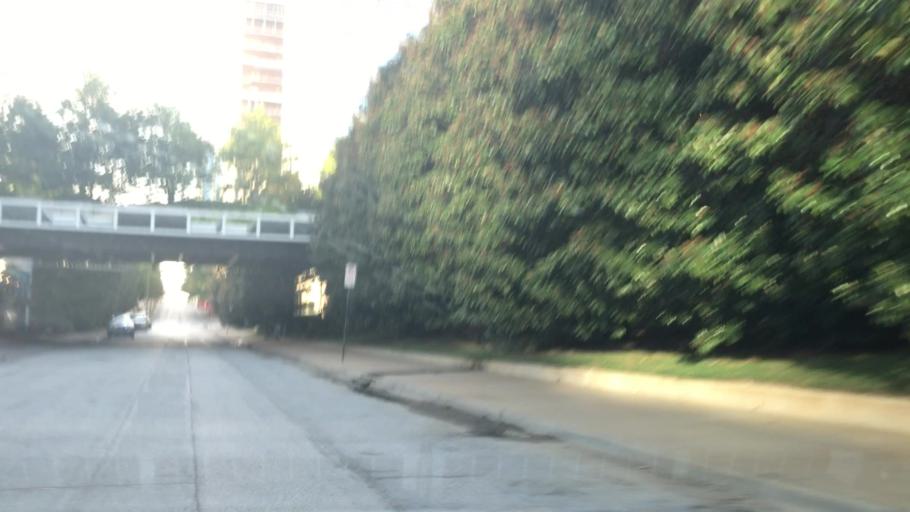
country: US
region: Texas
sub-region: Dallas County
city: Dallas
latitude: 32.7930
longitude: -96.8071
